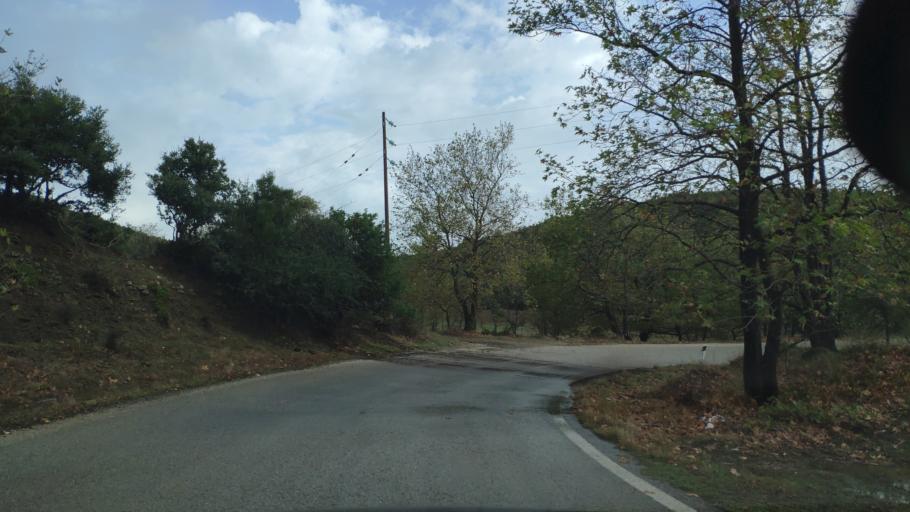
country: GR
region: West Greece
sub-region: Nomos Aitolias kai Akarnanias
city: Sardinia
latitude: 38.8791
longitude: 21.2632
